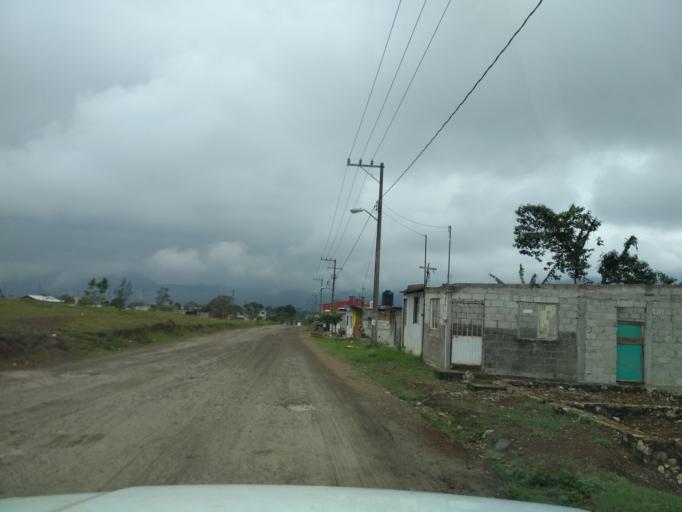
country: MX
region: Veracruz
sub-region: Cordoba
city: San Jose de Tapia
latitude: 18.8478
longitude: -96.9680
